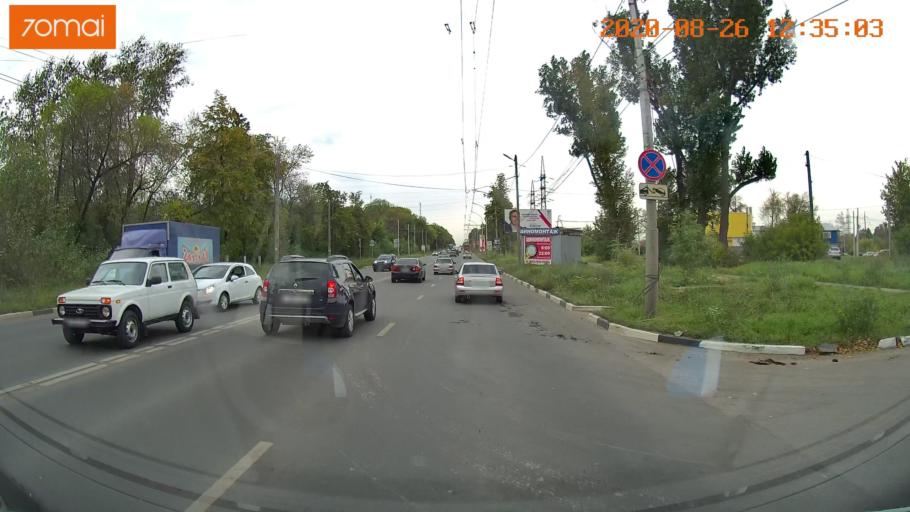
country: RU
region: Rjazan
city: Ryazan'
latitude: 54.5927
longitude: 39.7695
